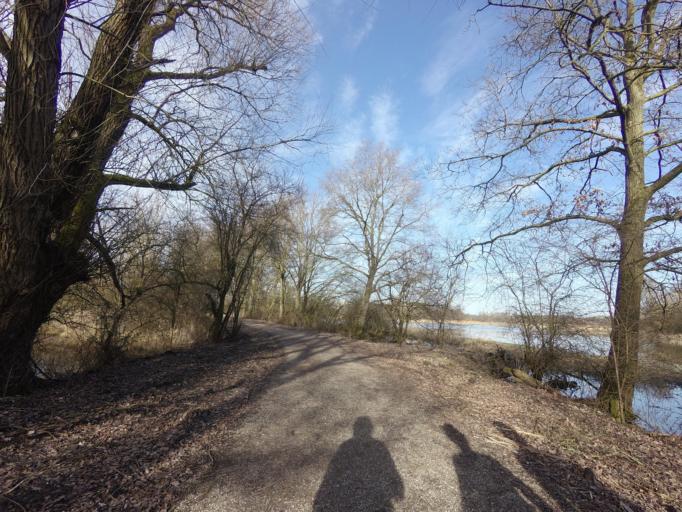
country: NL
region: North Holland
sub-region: Gemeente Naarden
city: Naarden
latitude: 52.3374
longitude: 5.1739
